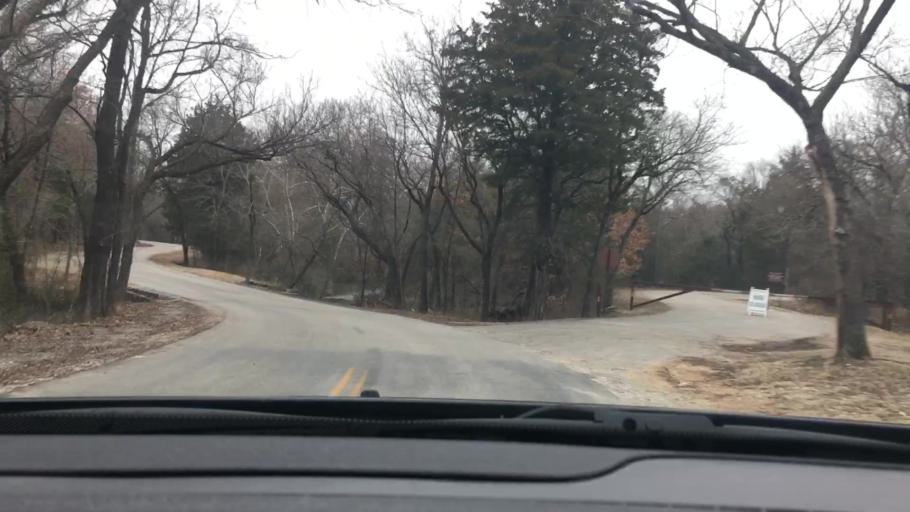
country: US
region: Oklahoma
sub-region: Murray County
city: Sulphur
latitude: 34.5030
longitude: -96.9654
